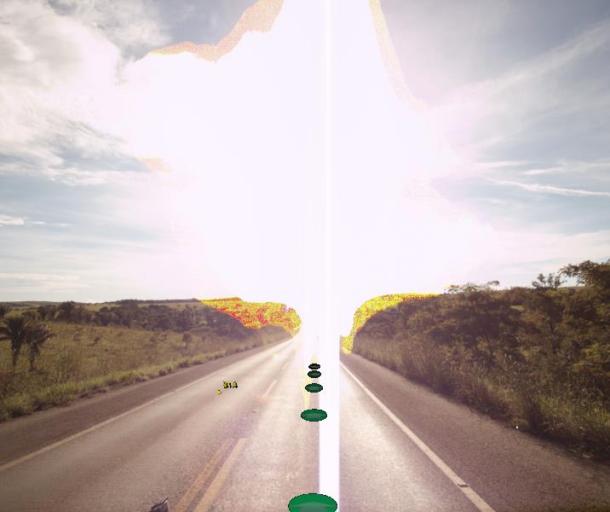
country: BR
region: Goias
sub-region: Abadiania
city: Abadiania
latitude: -15.7723
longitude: -48.4638
